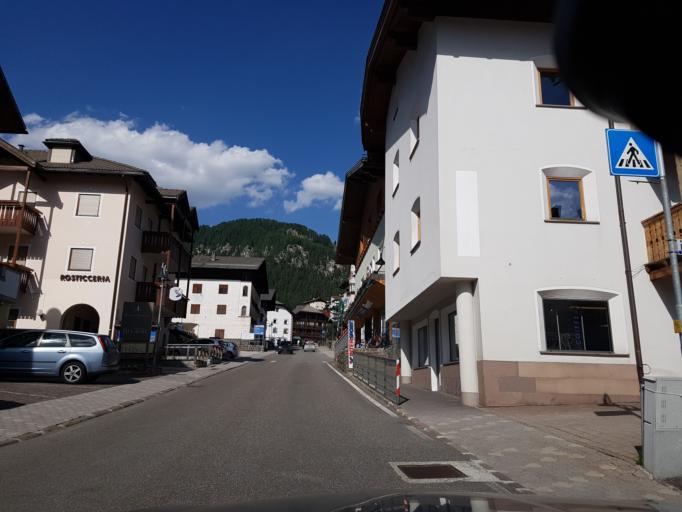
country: IT
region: Trentino-Alto Adige
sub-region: Bolzano
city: Santa Cristina Valgardena
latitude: 46.5583
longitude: 11.7260
